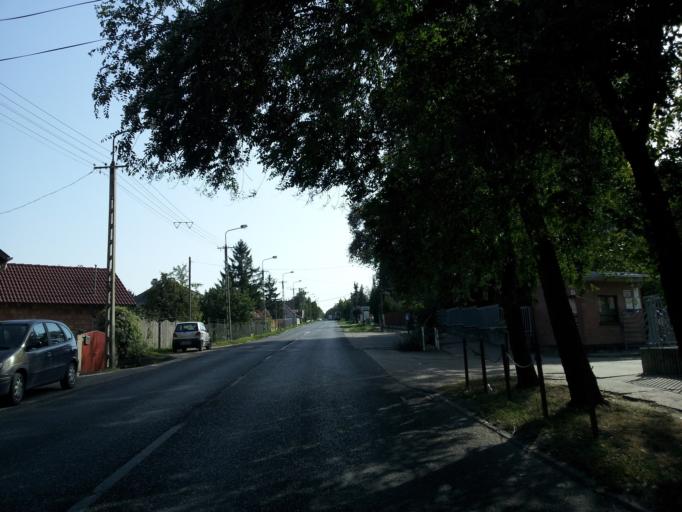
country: HU
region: Pest
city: Erd
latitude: 47.3752
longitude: 18.9164
